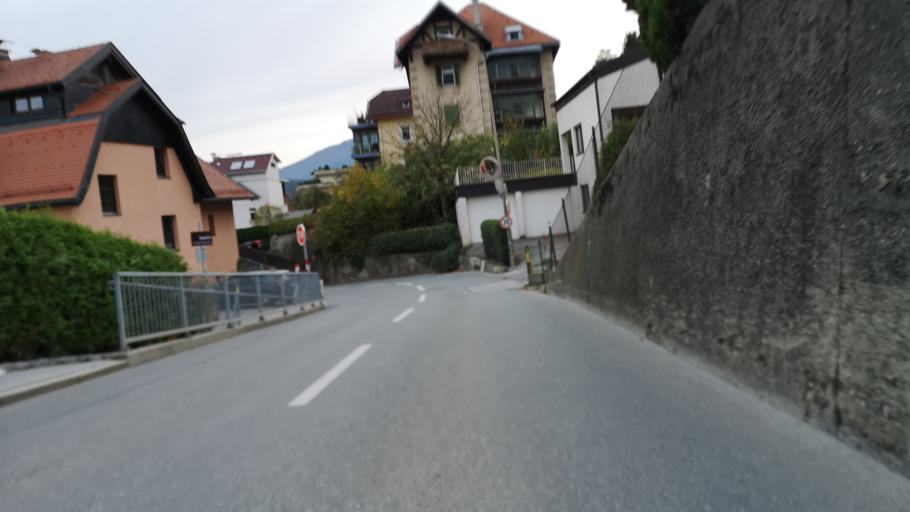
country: AT
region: Tyrol
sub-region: Innsbruck Stadt
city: Innsbruck
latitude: 47.2756
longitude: 11.3893
